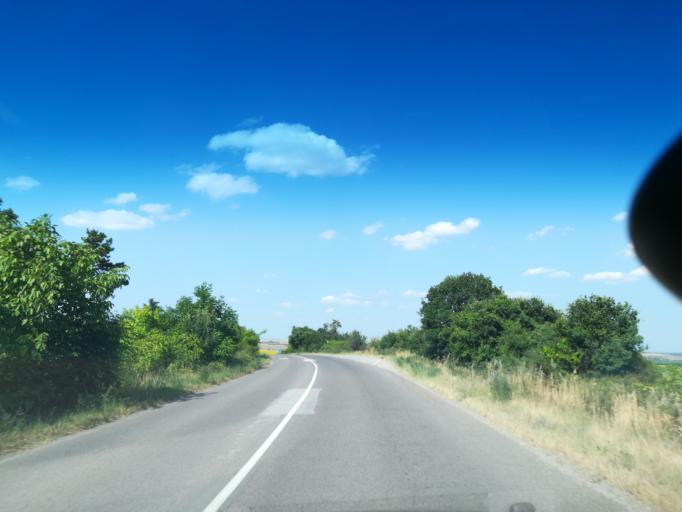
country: BG
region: Stara Zagora
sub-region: Obshtina Chirpan
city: Chirpan
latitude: 42.2192
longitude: 25.3826
